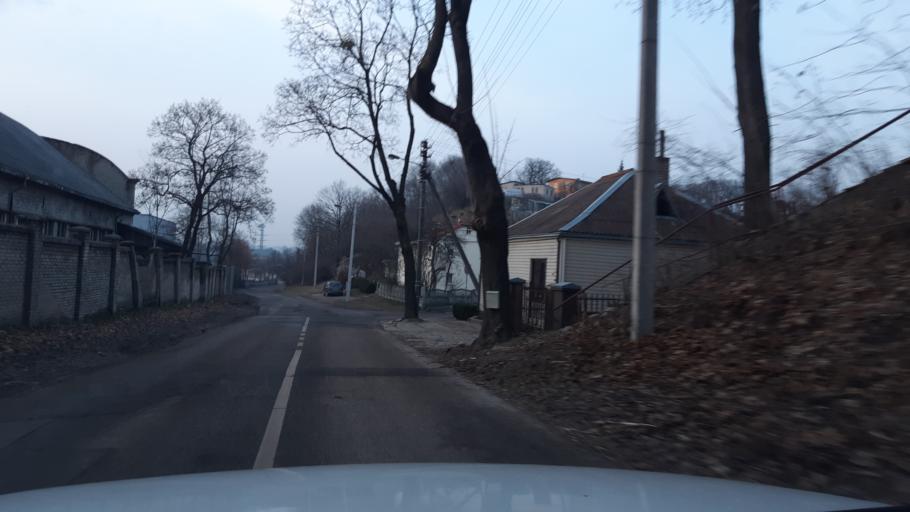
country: LT
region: Kauno apskritis
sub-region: Kaunas
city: Aleksotas
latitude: 54.8770
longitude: 23.9382
